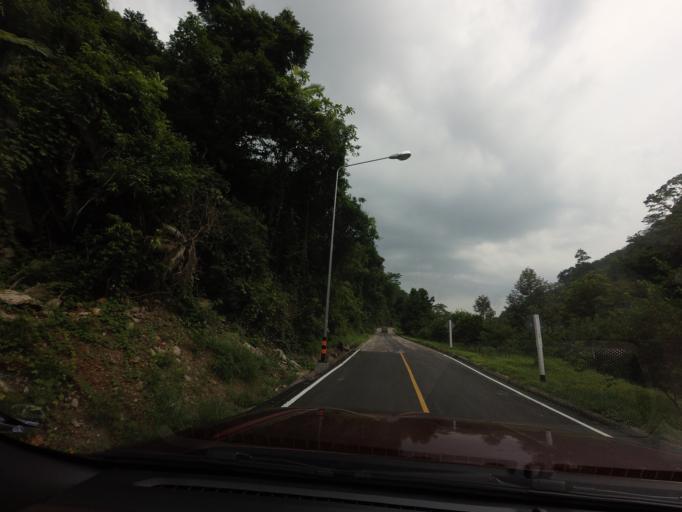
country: TH
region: Yala
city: Than To
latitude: 6.1359
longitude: 101.3019
